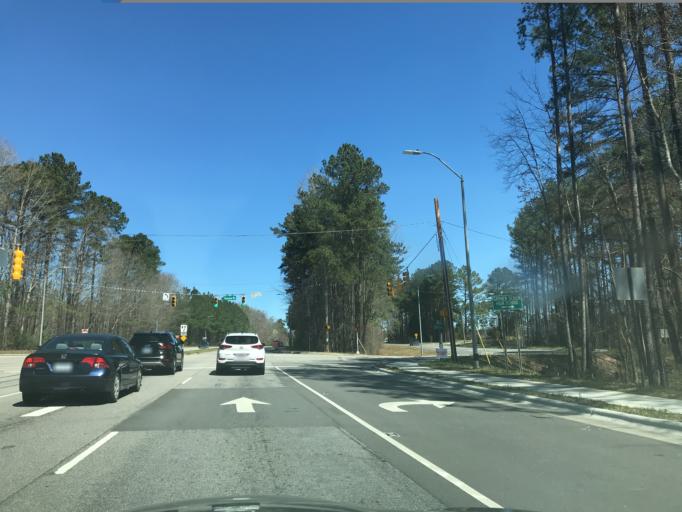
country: US
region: North Carolina
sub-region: Wake County
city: Garner
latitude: 35.7093
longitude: -78.6414
